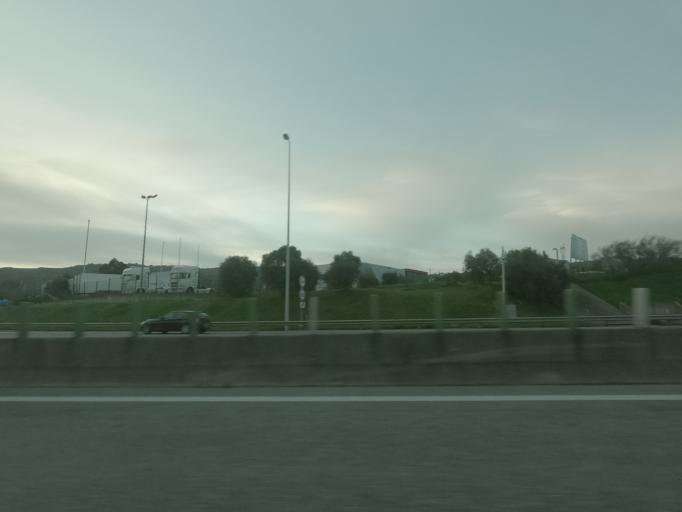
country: PT
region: Lisbon
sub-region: Vila Franca de Xira
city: Sobralinho
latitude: 38.8956
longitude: -9.0477
